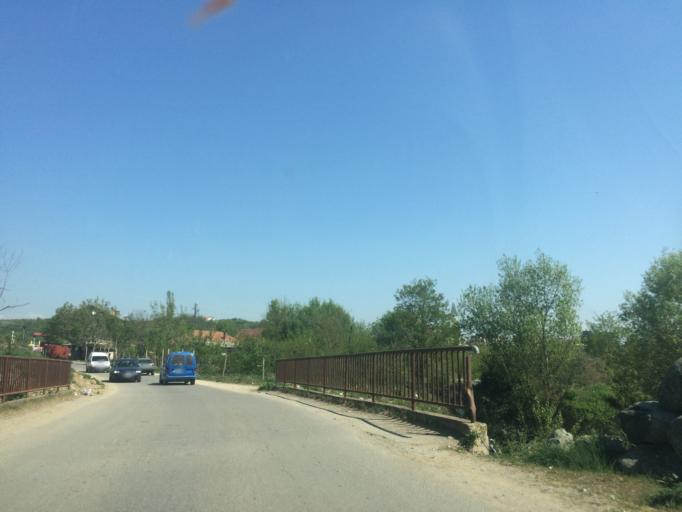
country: XK
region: Gjakova
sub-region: Komuna e Gjakoves
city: Gjakove
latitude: 42.3679
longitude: 20.4202
